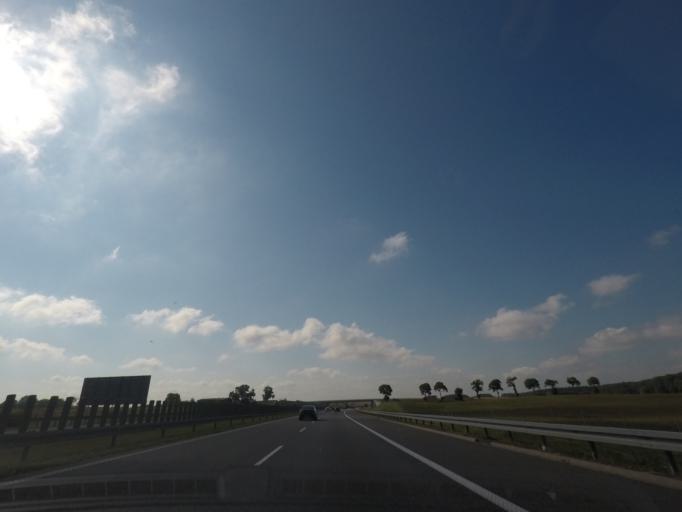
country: PL
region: Pomeranian Voivodeship
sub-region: Powiat tczewski
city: Pelplin
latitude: 53.9161
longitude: 18.6446
